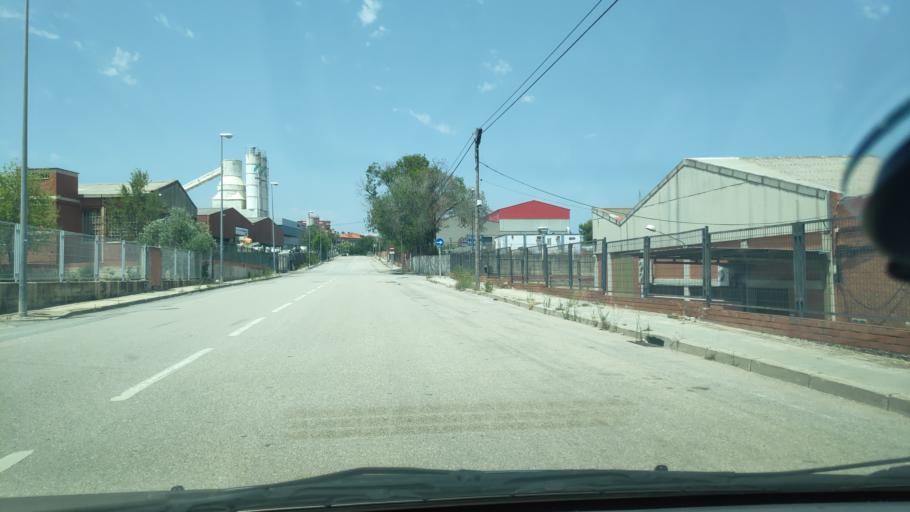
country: ES
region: Catalonia
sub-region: Provincia de Barcelona
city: Terrassa
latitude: 41.5509
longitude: 2.0363
